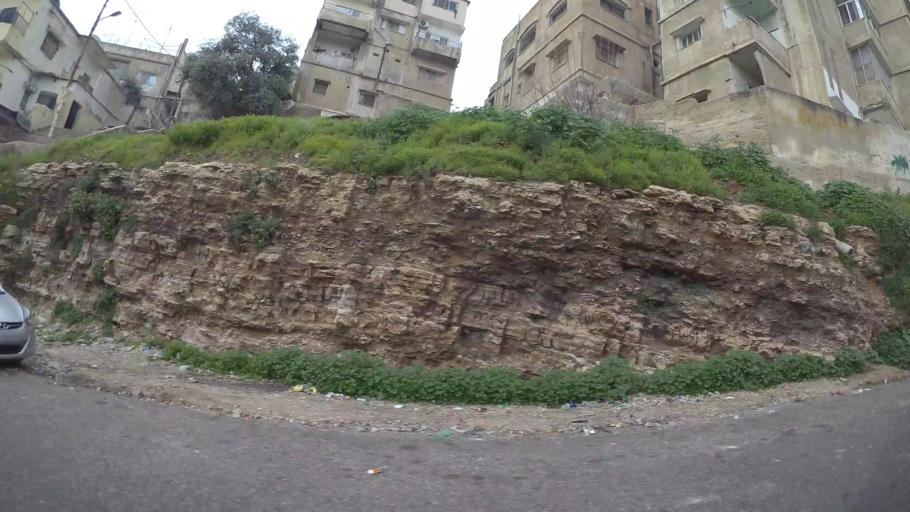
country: JO
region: Amman
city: Amman
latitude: 31.9657
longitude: 35.9296
